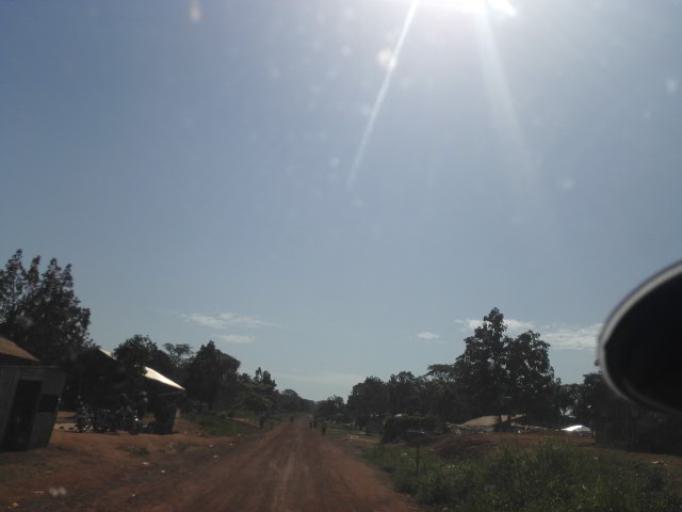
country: CD
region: Eastern Province
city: Wamba
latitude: 1.4095
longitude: 28.0825
